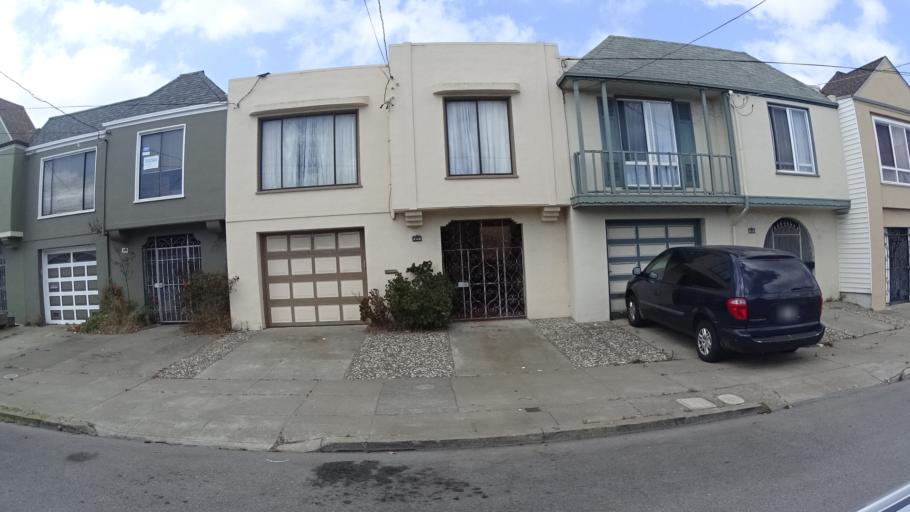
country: US
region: California
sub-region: San Mateo County
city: Daly City
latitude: 37.7472
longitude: -122.5007
